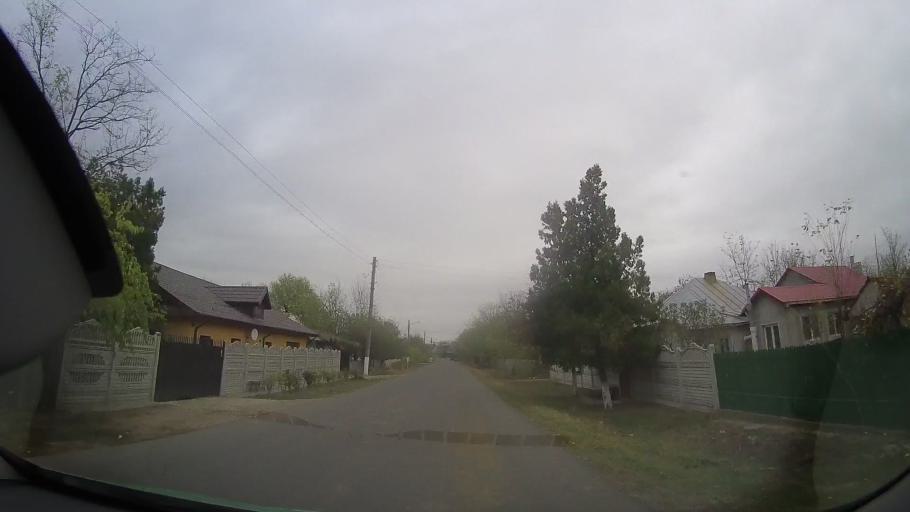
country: RO
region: Braila
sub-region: Comuna Ciocile
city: Ciocile
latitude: 44.7859
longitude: 27.2658
